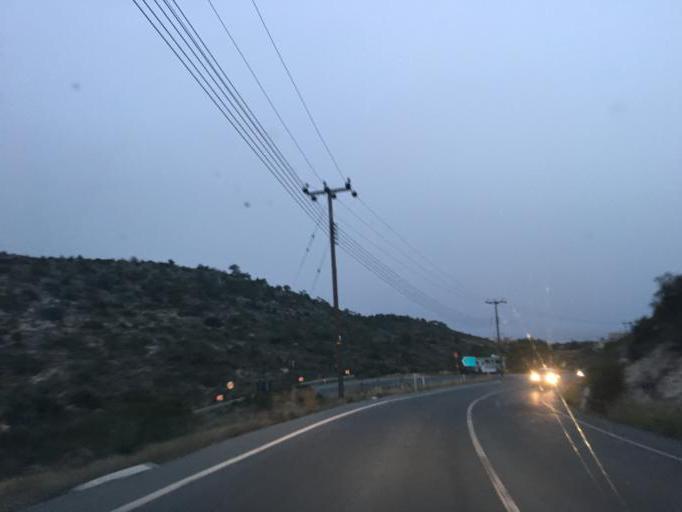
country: CY
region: Limassol
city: Parekklisha
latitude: 34.7226
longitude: 33.1640
